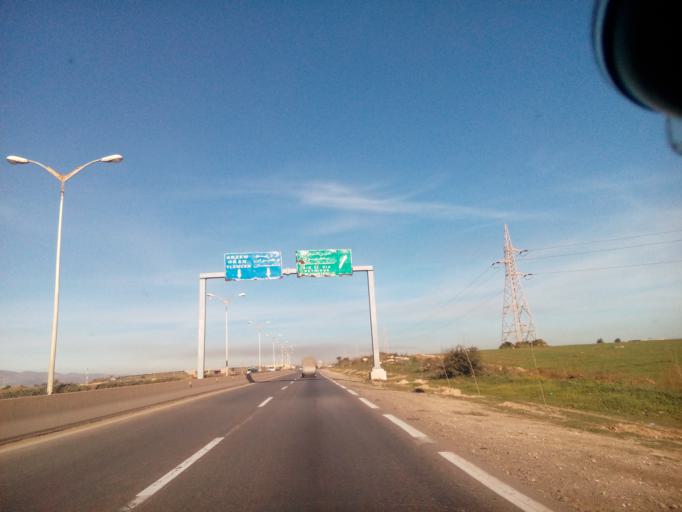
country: DZ
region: Oran
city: Ain el Bya
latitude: 35.7951
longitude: -0.2902
